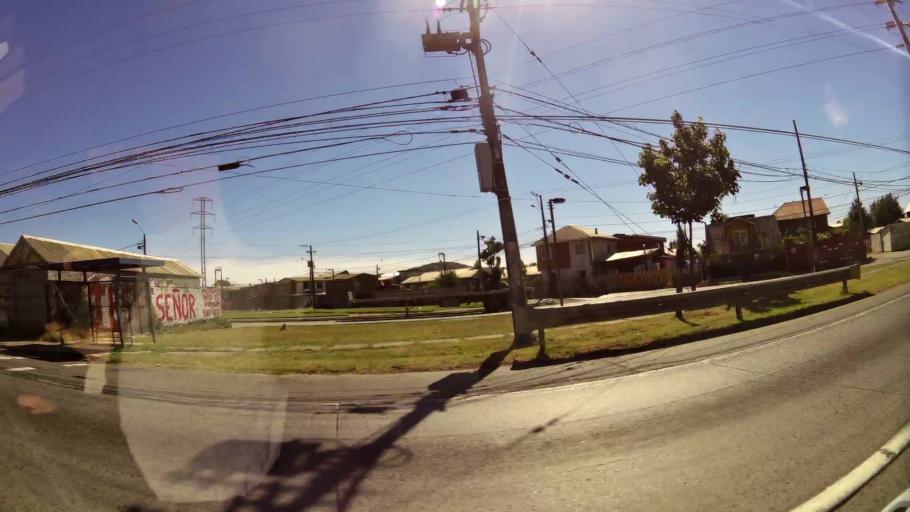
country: CL
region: Biobio
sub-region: Provincia de Concepcion
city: Concepcion
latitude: -36.7970
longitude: -73.0258
